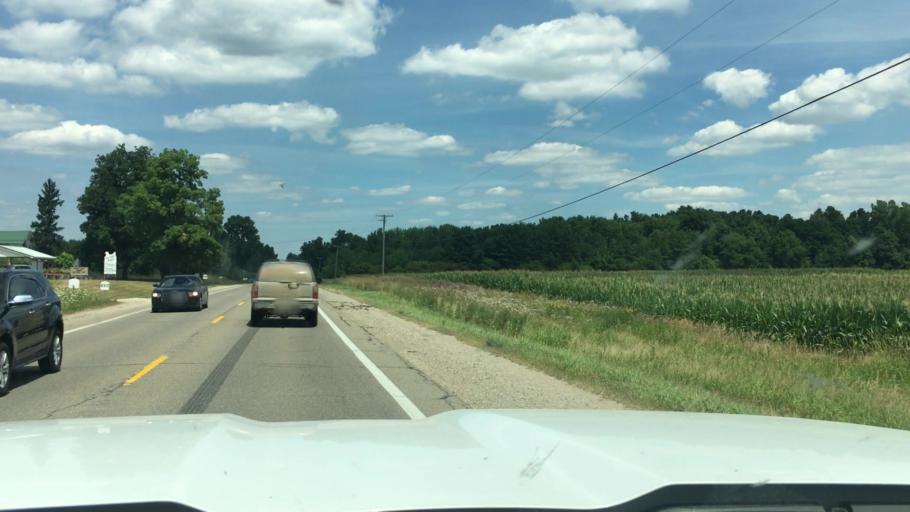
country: US
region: Michigan
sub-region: Lapeer County
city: Barnes Lake-Millers Lake
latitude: 43.1210
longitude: -83.3096
